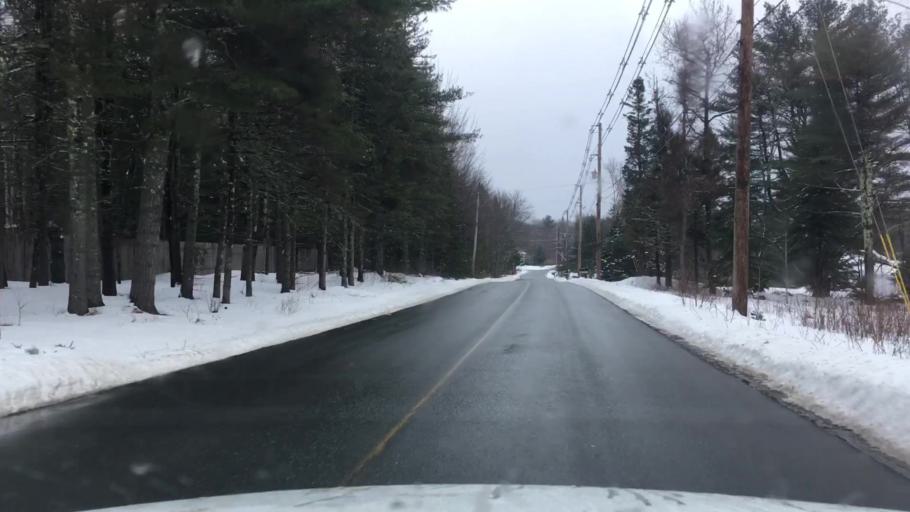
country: US
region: Maine
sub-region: Hancock County
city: Trenton
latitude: 44.4141
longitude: -68.3346
